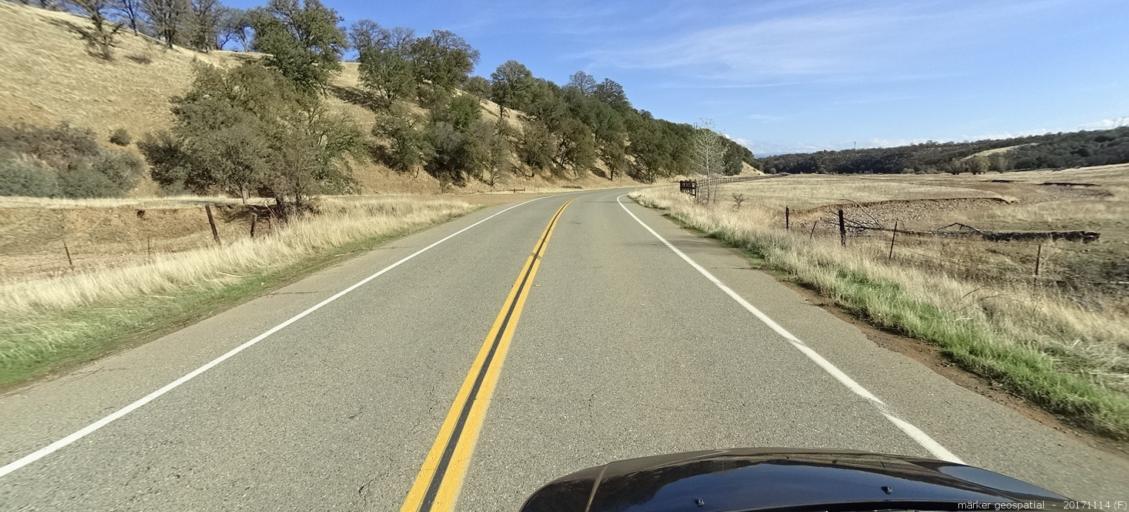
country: US
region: California
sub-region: Shasta County
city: Anderson
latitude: 40.4337
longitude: -122.3165
